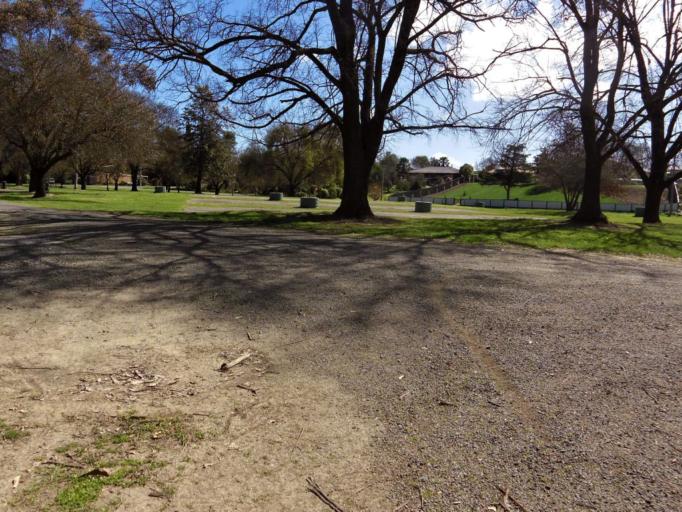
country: AU
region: Victoria
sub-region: Murrindindi
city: Alexandra
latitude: -37.1879
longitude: 145.7119
